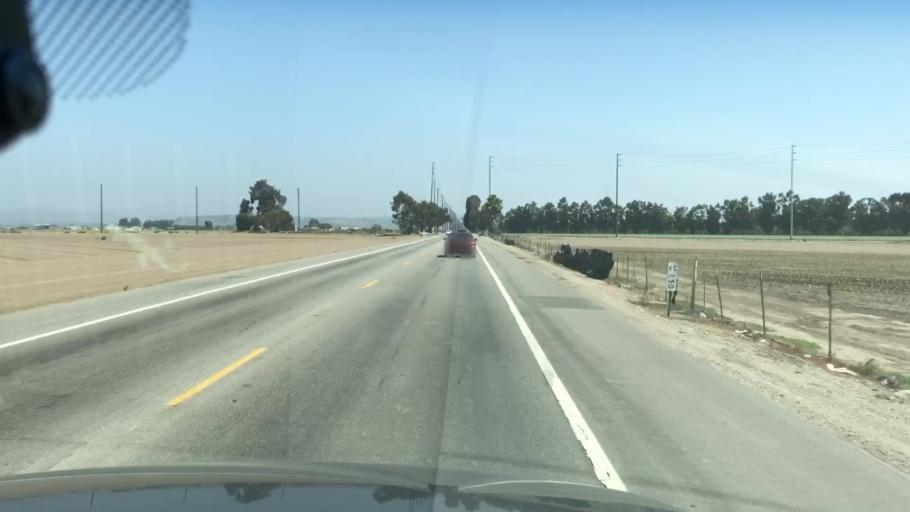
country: US
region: California
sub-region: Ventura County
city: Oxnard
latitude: 34.1791
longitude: -119.1209
